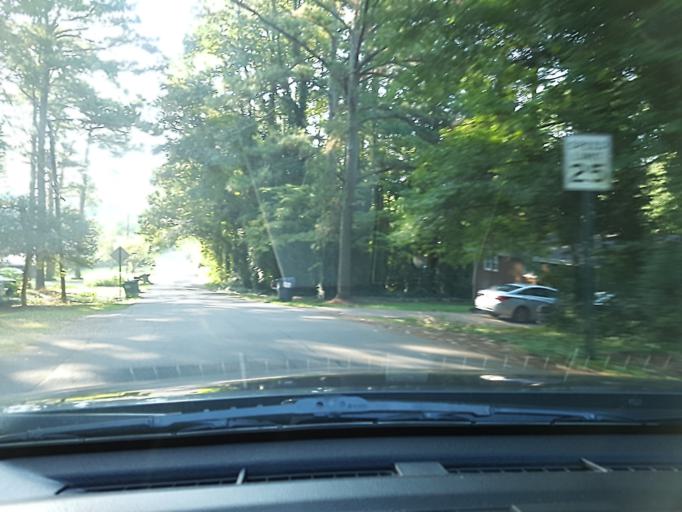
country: US
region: Georgia
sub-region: Cobb County
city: Mableton
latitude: 33.8192
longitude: -84.5885
